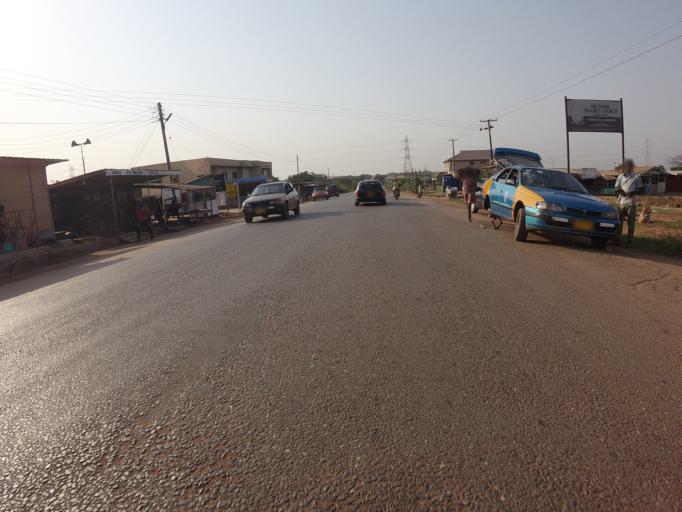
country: GH
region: Greater Accra
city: Tema
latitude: 5.6921
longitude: 0.0525
